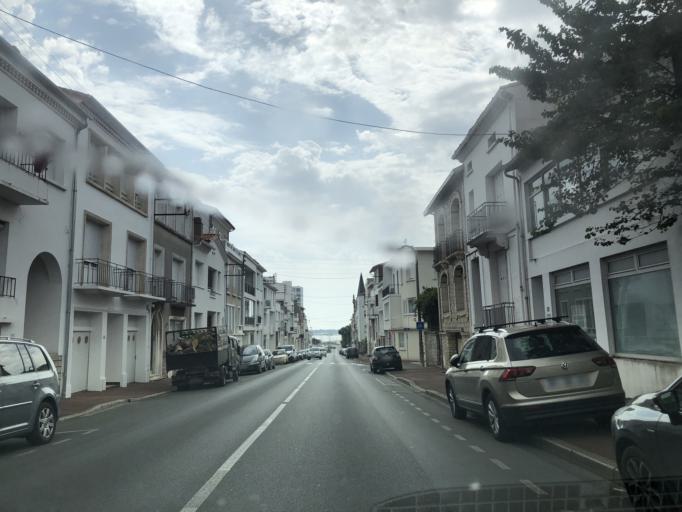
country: FR
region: Poitou-Charentes
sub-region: Departement de la Charente-Maritime
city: Royan
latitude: 45.6214
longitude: -1.0380
